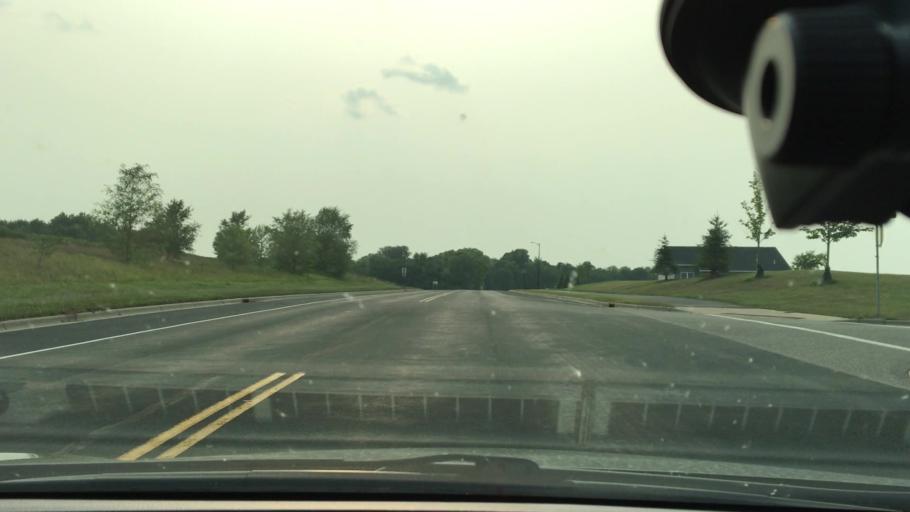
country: US
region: Minnesota
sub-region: Wright County
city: Otsego
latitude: 45.2597
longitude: -93.5871
